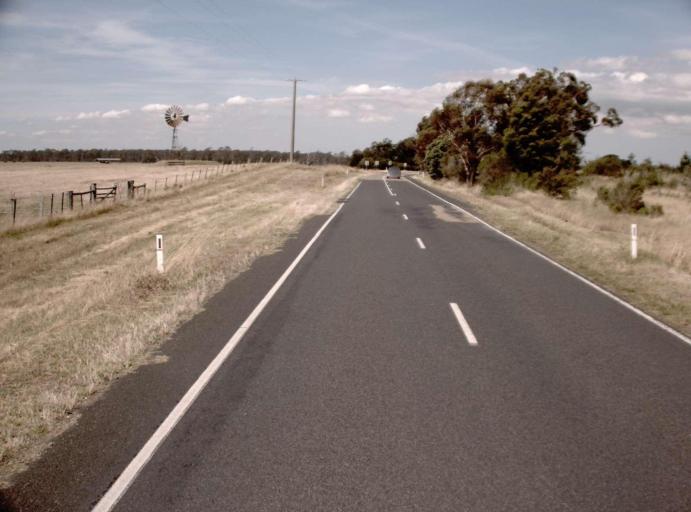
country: AU
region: Victoria
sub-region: Wellington
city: Sale
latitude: -38.1625
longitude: 146.9062
